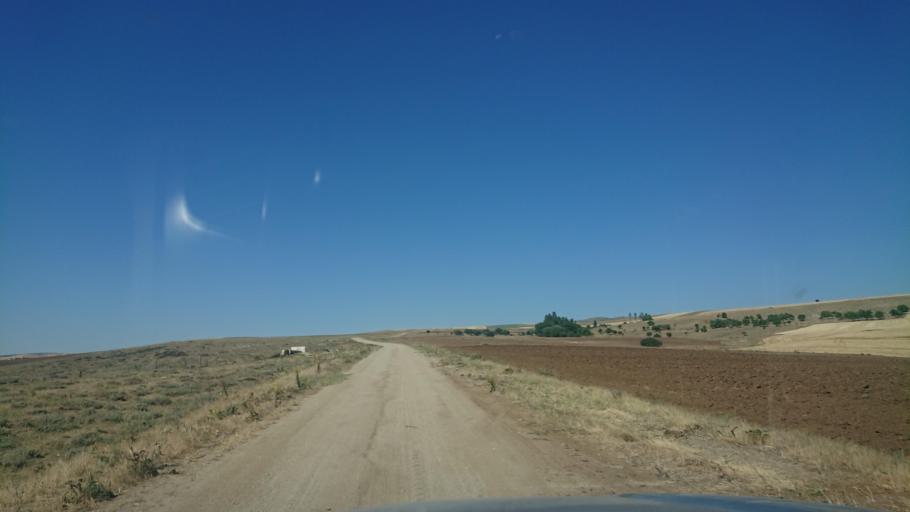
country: TR
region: Aksaray
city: Sariyahsi
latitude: 38.9360
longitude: 33.8649
